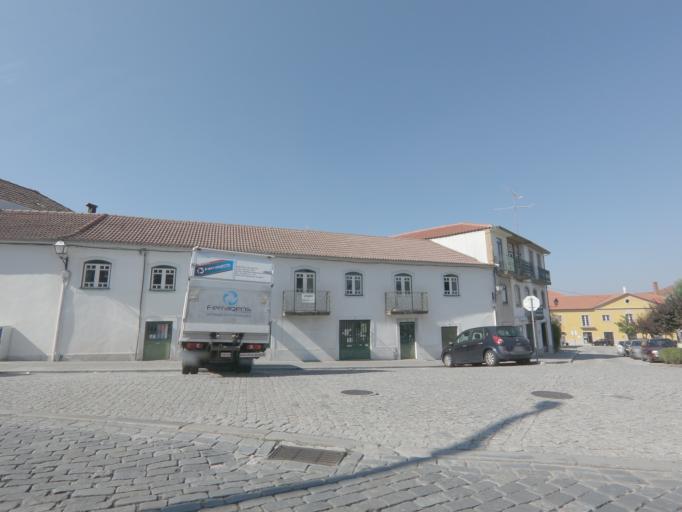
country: PT
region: Viseu
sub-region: Moimenta da Beira
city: Moimenta da Beira
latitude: 40.9802
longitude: -7.6136
